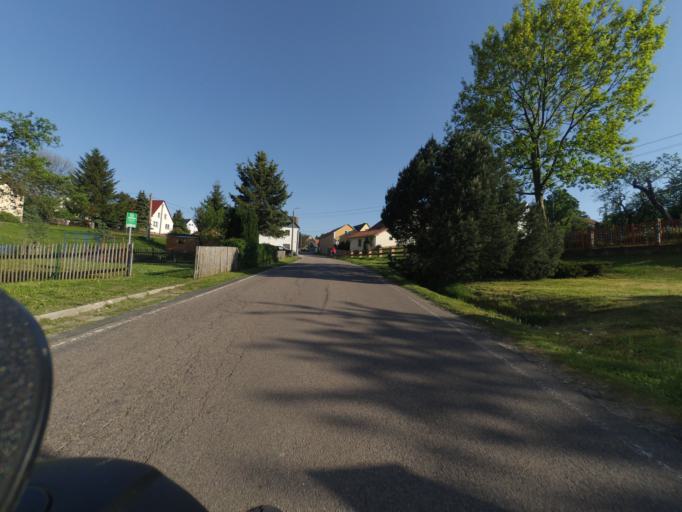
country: DE
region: Saxony
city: Obercunnersdorf
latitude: 50.8868
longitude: 13.5839
